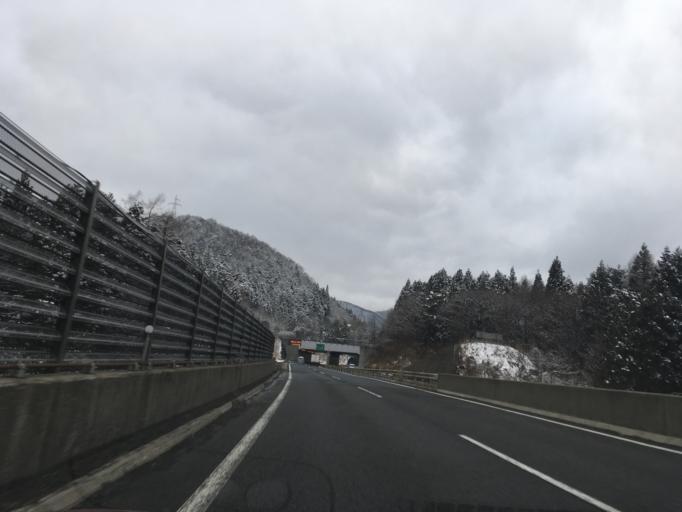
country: JP
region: Yamagata
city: Yamagata-shi
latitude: 38.2202
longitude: 140.5167
